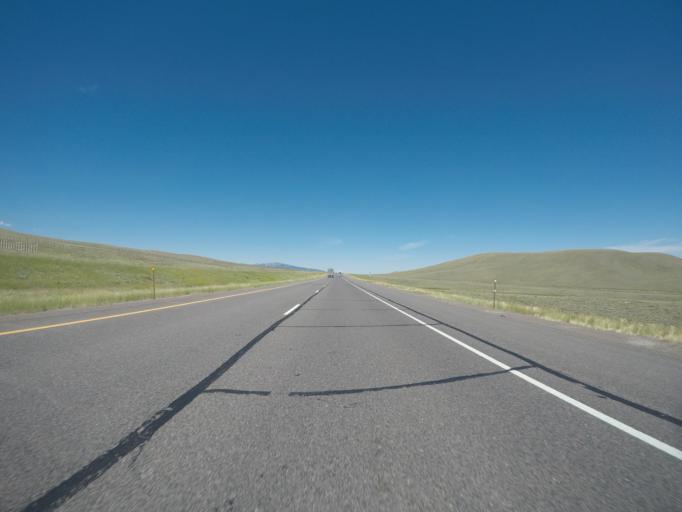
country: US
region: Wyoming
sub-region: Carbon County
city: Saratoga
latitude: 41.6241
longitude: -106.2510
